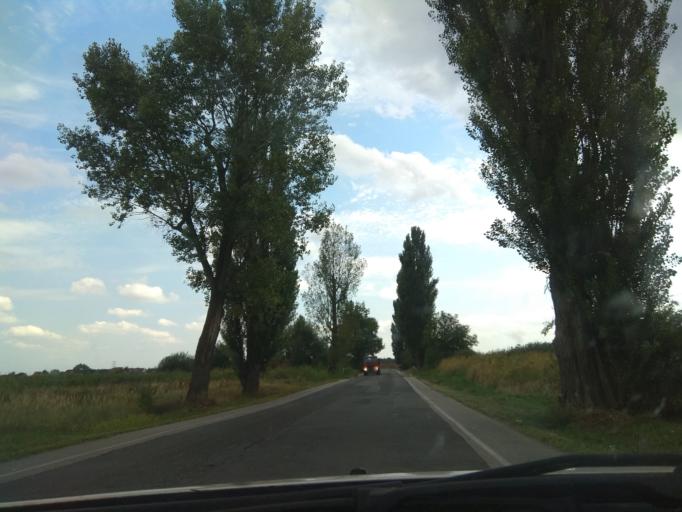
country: HU
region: Borsod-Abauj-Zemplen
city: Malyi
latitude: 48.0520
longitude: 20.8337
